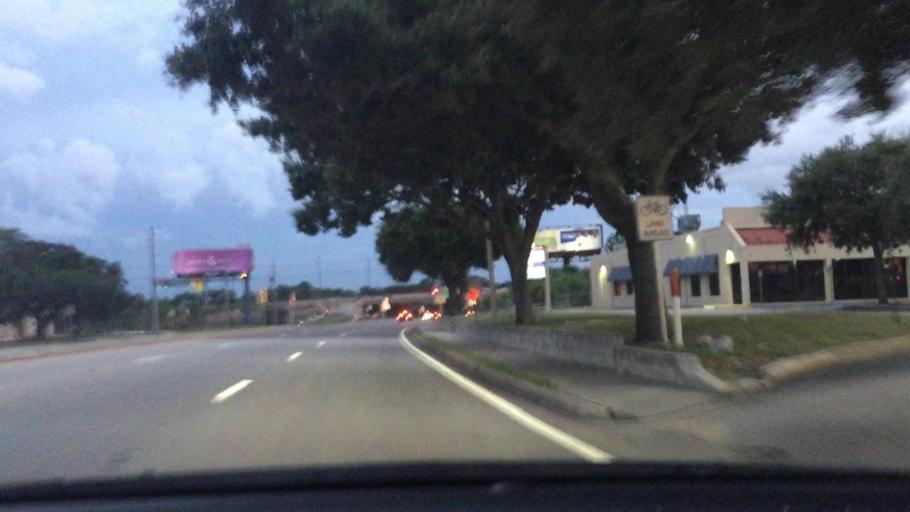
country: US
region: Florida
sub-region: Orange County
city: Pine Hills
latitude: 28.5515
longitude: -81.4567
